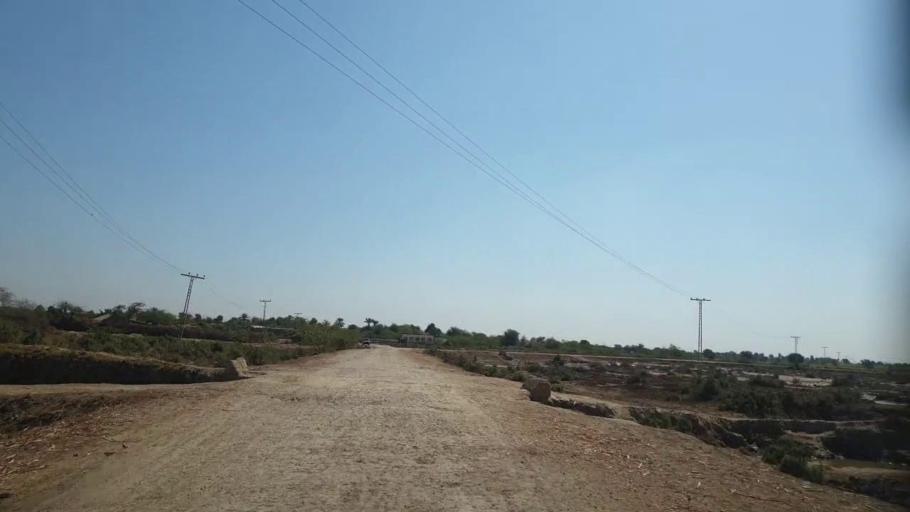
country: PK
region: Sindh
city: Mirpur Khas
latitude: 25.5835
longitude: 69.1117
